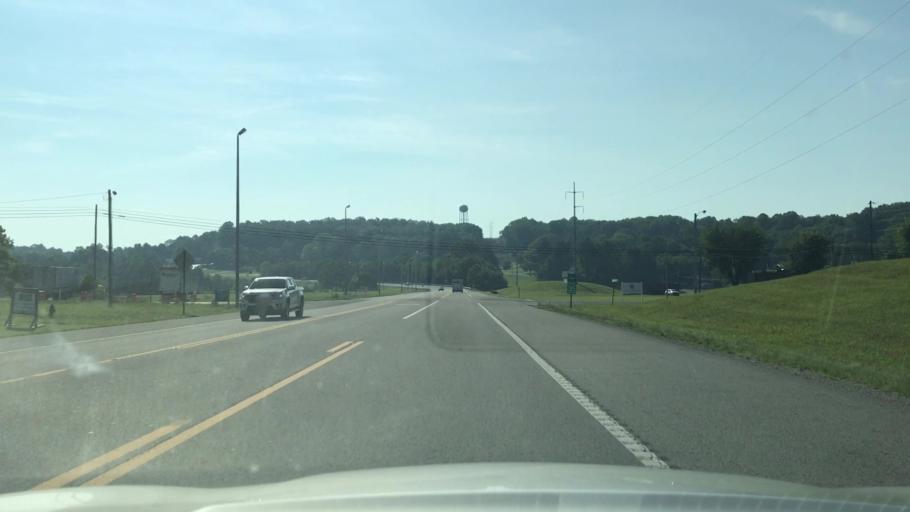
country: US
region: Tennessee
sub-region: Overton County
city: Livingston
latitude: 36.3980
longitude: -85.3189
